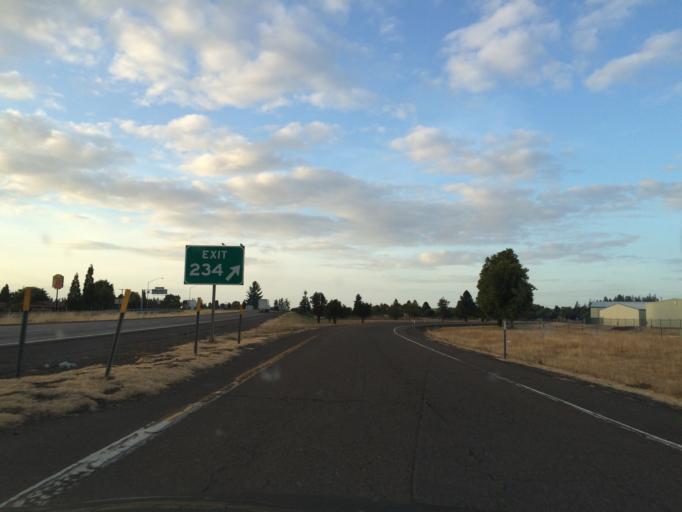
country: US
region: Oregon
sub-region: Linn County
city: Millersburg
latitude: 44.6402
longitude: -123.0622
